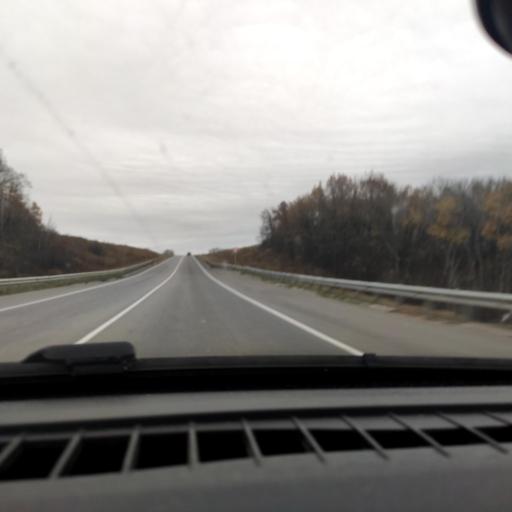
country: RU
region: Voronezj
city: Strelitsa
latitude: 51.5199
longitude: 38.9679
